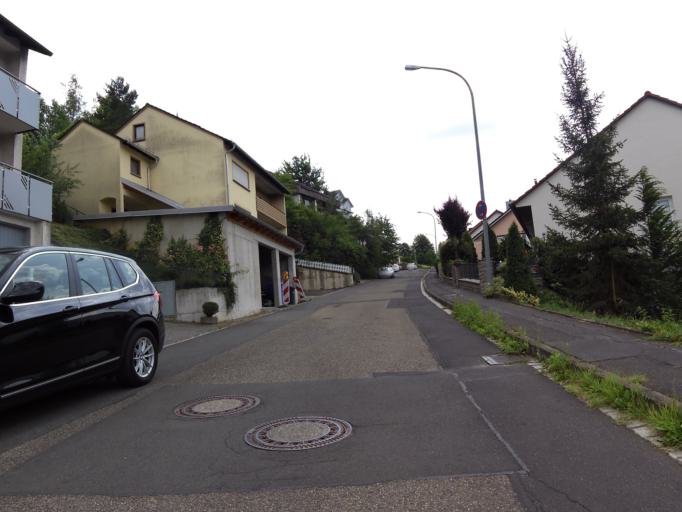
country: DE
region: Bavaria
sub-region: Regierungsbezirk Unterfranken
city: Gerbrunn
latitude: 49.7683
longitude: 9.9946
